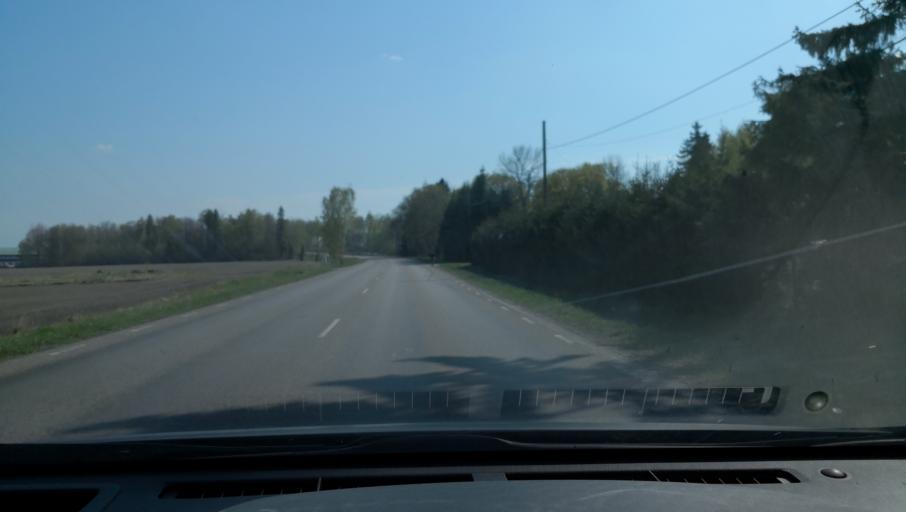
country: SE
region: Vaestmanland
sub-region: Sala Kommun
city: Sala
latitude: 59.9481
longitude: 16.6163
